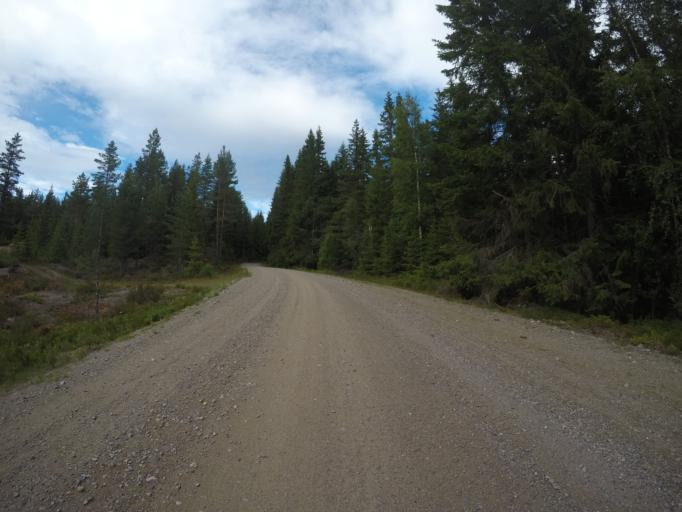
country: SE
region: OErebro
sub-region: Hallefors Kommun
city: Haellefors
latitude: 60.0113
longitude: 14.4331
